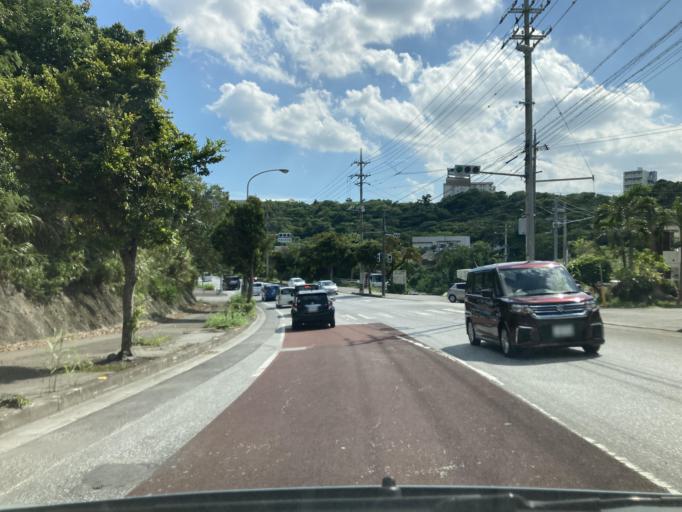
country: JP
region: Okinawa
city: Ginowan
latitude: 26.2485
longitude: 127.7574
